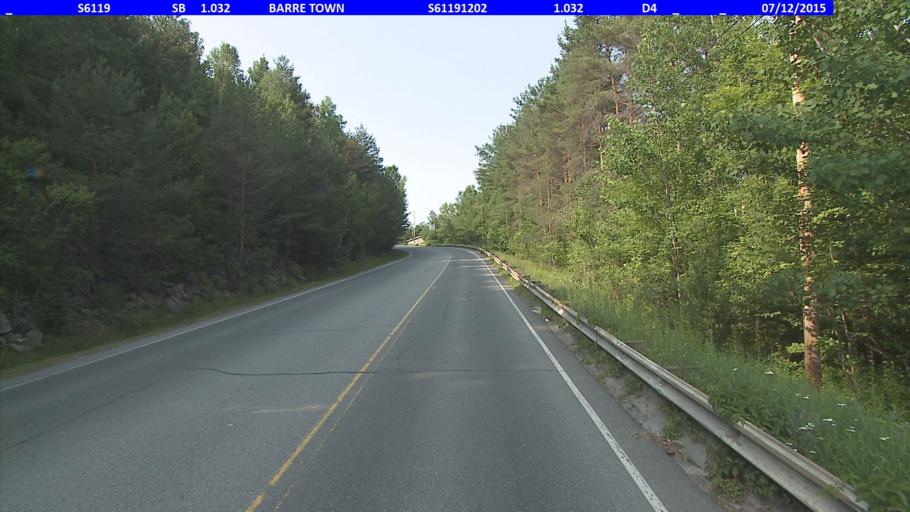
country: US
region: Vermont
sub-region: Washington County
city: South Barre
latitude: 44.1816
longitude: -72.4947
